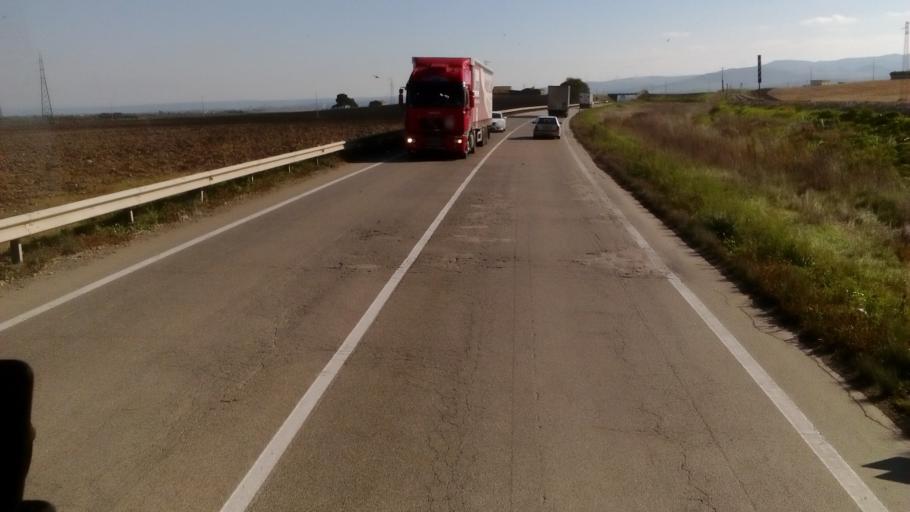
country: IT
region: Apulia
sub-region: Provincia di Foggia
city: Candela
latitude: 41.1174
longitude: 15.5774
